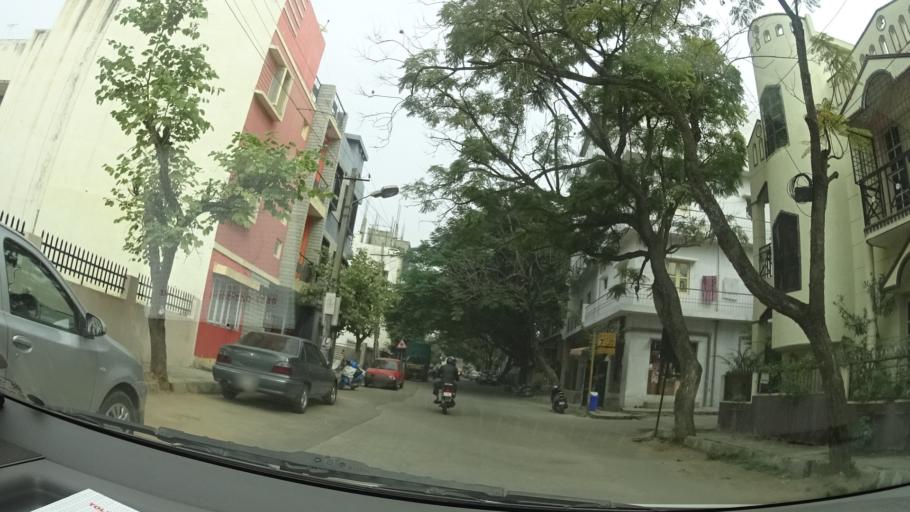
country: IN
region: Karnataka
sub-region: Bangalore Urban
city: Bangalore
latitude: 13.0241
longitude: 77.6286
